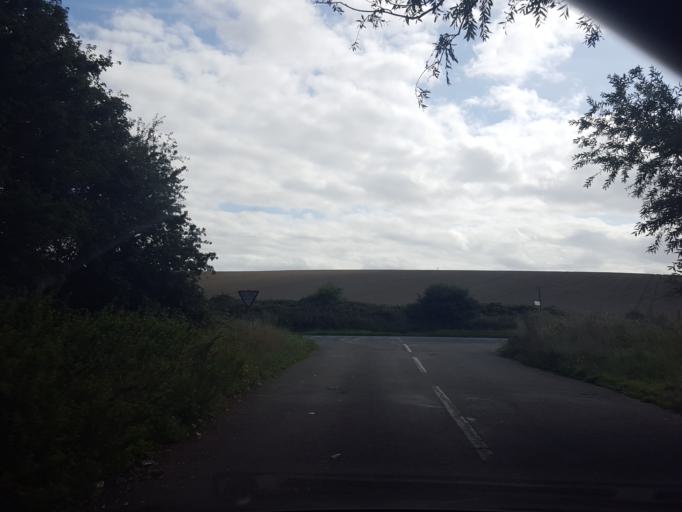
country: GB
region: England
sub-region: Suffolk
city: Shotley Gate
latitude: 51.9257
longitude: 1.2039
